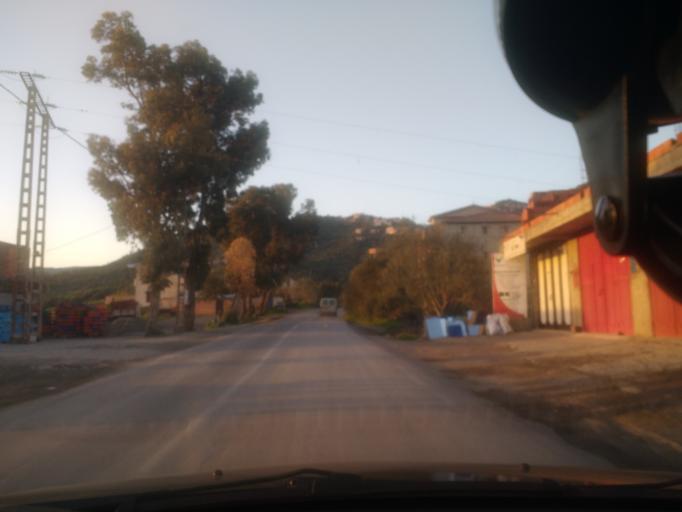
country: DZ
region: Boumerdes
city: Makouda
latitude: 36.7749
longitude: 4.0649
